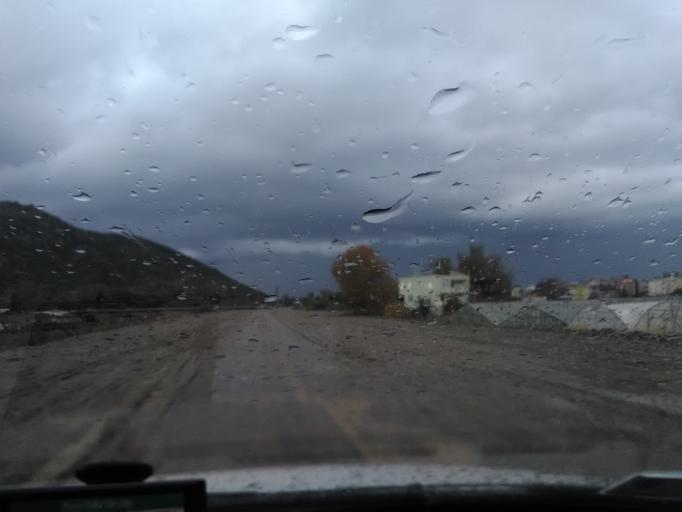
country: TR
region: Antalya
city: Gazipasa
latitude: 36.2616
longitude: 32.2929
